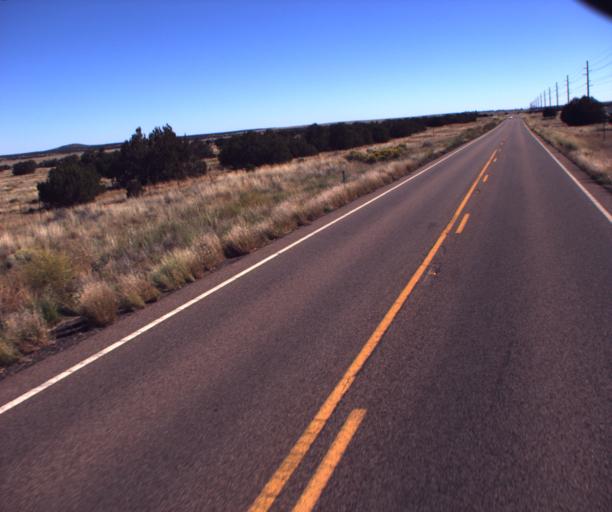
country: US
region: Arizona
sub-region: Navajo County
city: Taylor
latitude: 34.4821
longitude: -110.3009
